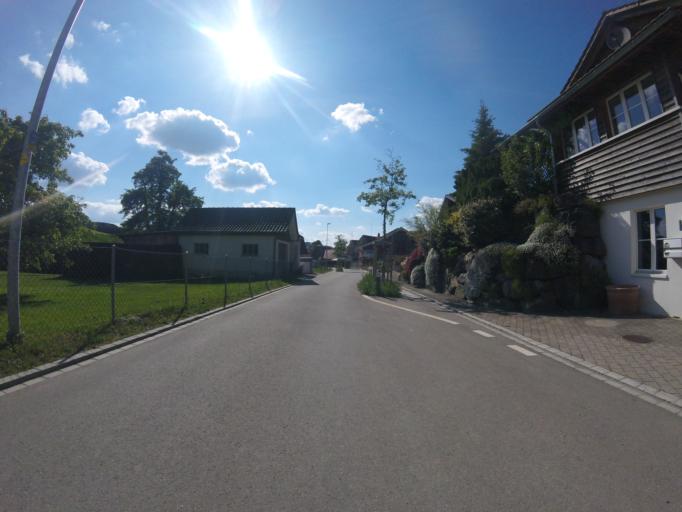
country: CH
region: Saint Gallen
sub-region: Wahlkreis Wil
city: Degersheim
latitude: 47.3949
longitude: 9.2045
